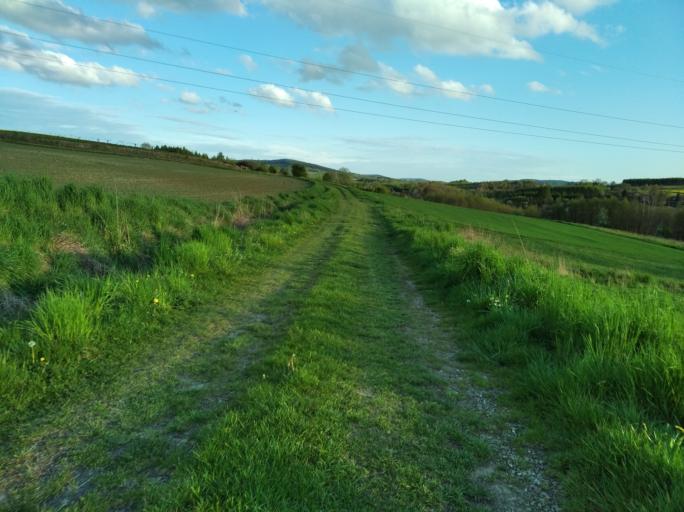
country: PL
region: Subcarpathian Voivodeship
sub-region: Powiat strzyzowski
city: Wysoka Strzyzowska
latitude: 49.8623
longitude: 21.7547
